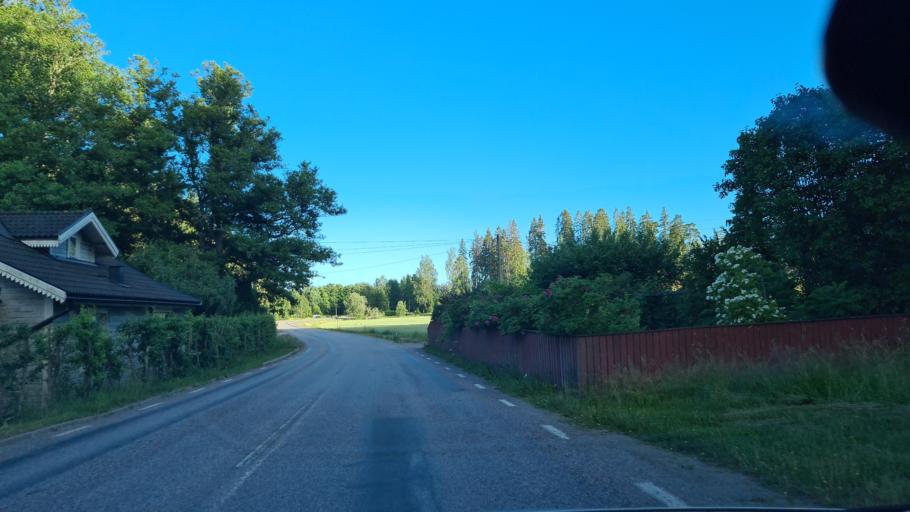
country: SE
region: Soedermanland
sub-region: Gnesta Kommun
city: Gnesta
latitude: 59.0321
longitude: 17.3331
